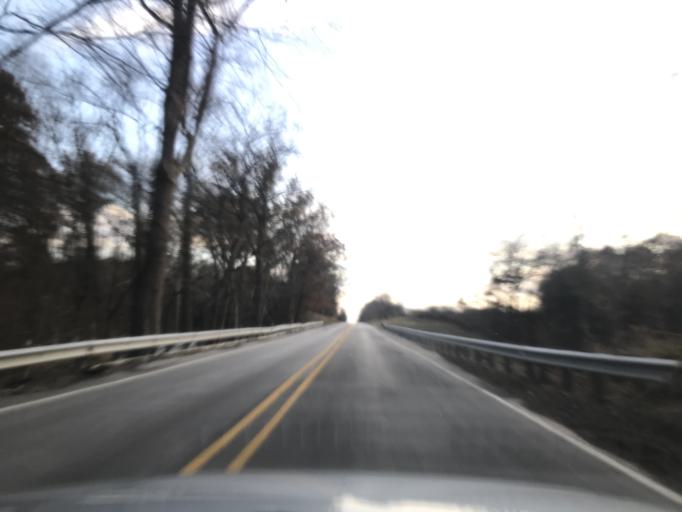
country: US
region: Illinois
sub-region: Henderson County
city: Oquawka
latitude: 40.9849
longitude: -90.8638
